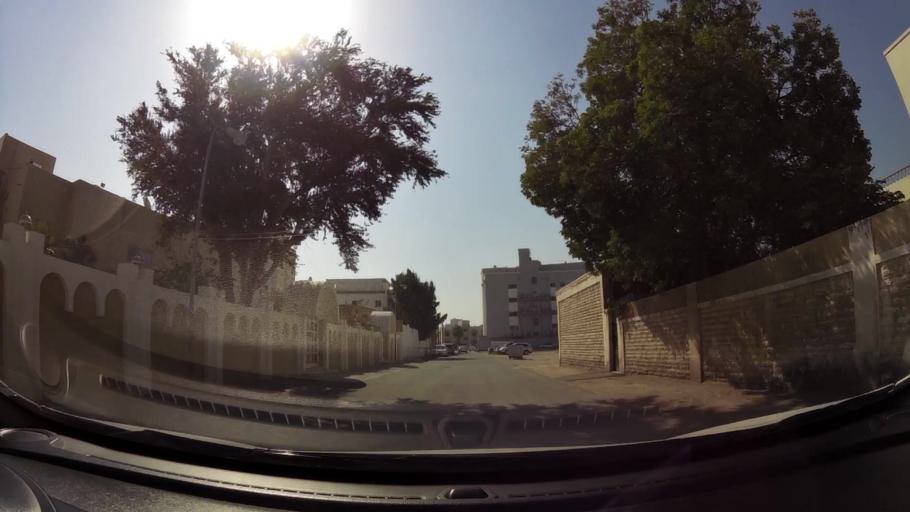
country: BH
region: Manama
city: Manama
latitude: 26.2095
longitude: 50.5888
